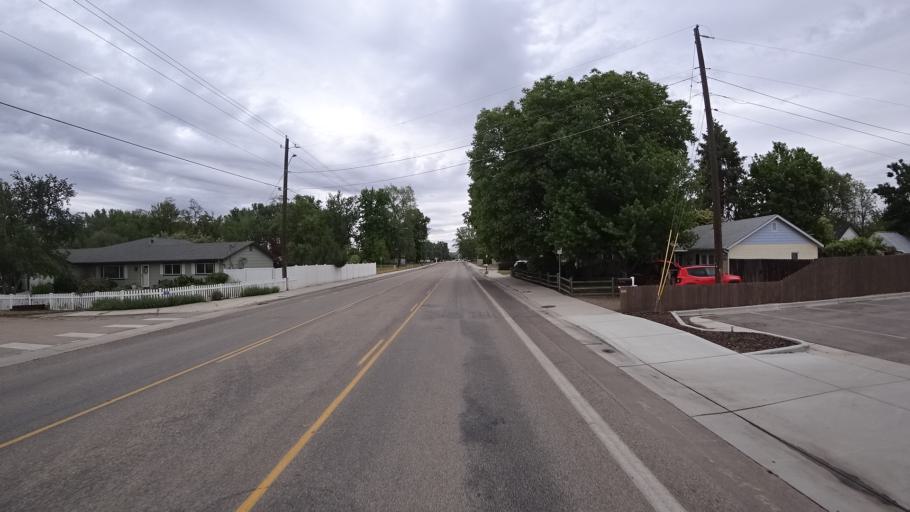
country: US
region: Idaho
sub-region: Ada County
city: Star
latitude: 43.6937
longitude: -116.4933
